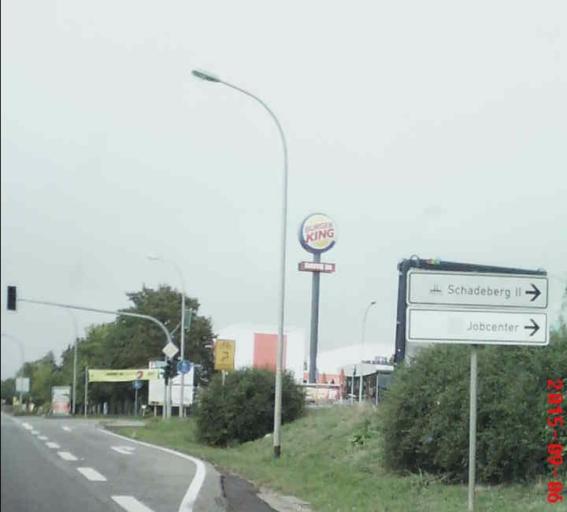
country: DE
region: Thuringia
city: Muehlhausen
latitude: 51.1968
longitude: 10.4832
